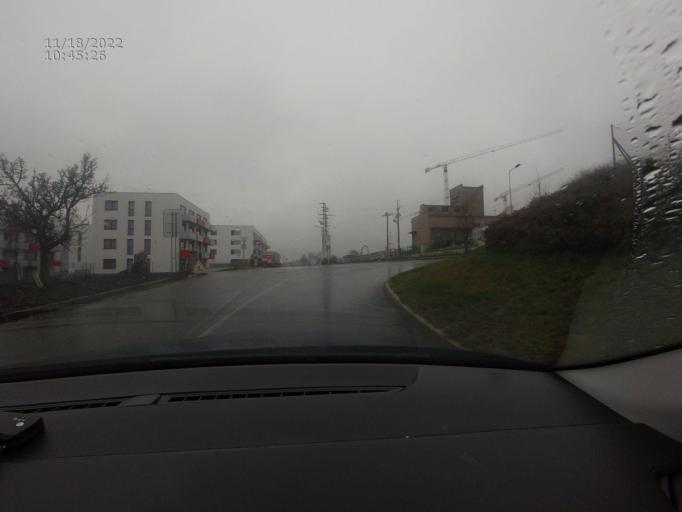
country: CZ
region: Central Bohemia
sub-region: Okres Beroun
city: Horovice
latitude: 49.8422
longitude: 13.9160
